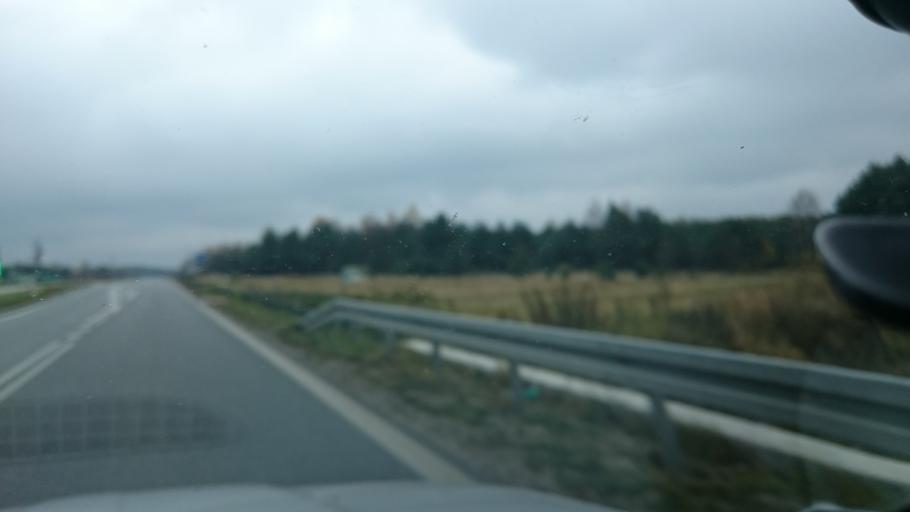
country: PL
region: Swietokrzyskie
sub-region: Powiat konecki
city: Konskie
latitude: 51.1360
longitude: 20.3628
